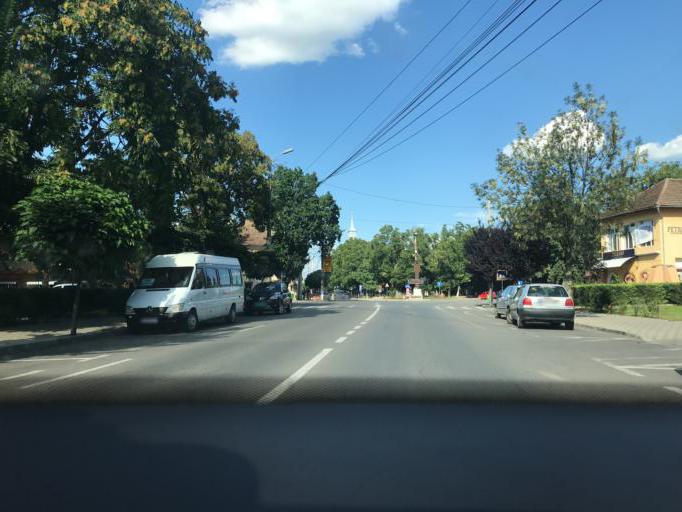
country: RO
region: Bihor
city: Margita
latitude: 47.3458
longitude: 22.3391
